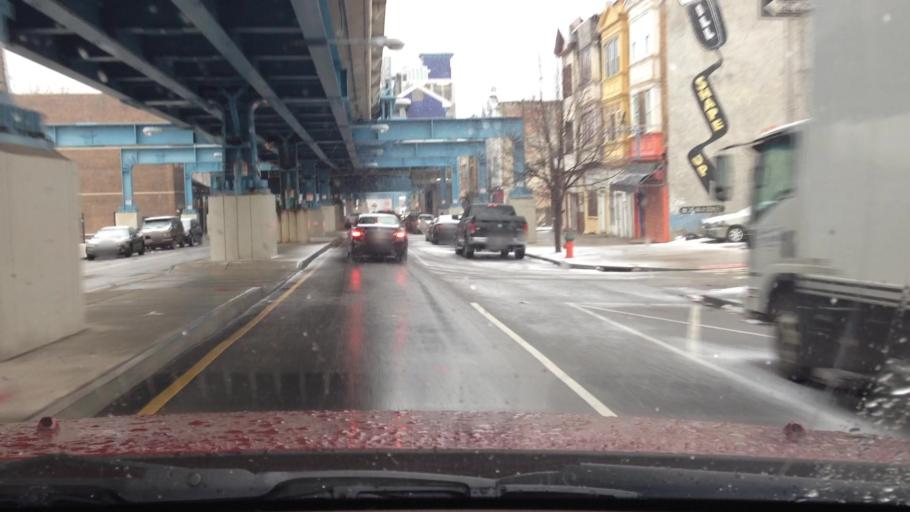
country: US
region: Pennsylvania
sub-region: Delaware County
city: Millbourne
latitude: 39.9625
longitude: -75.2451
